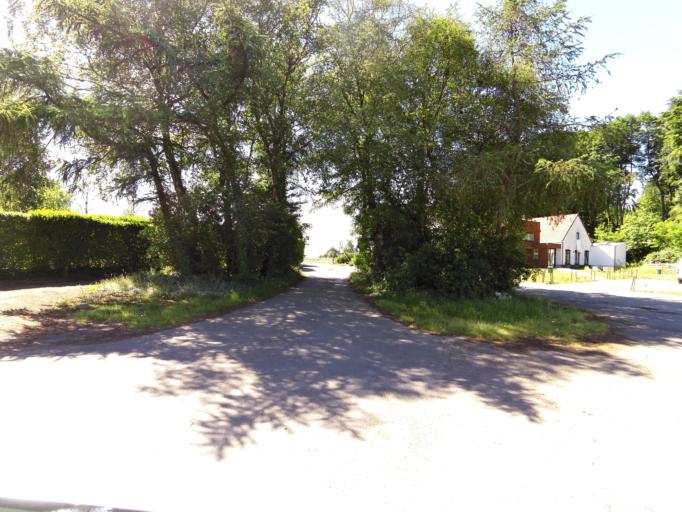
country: FR
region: Nord-Pas-de-Calais
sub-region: Departement du Nord
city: Saint-Jans-Cappel
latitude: 50.7869
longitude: 2.7621
